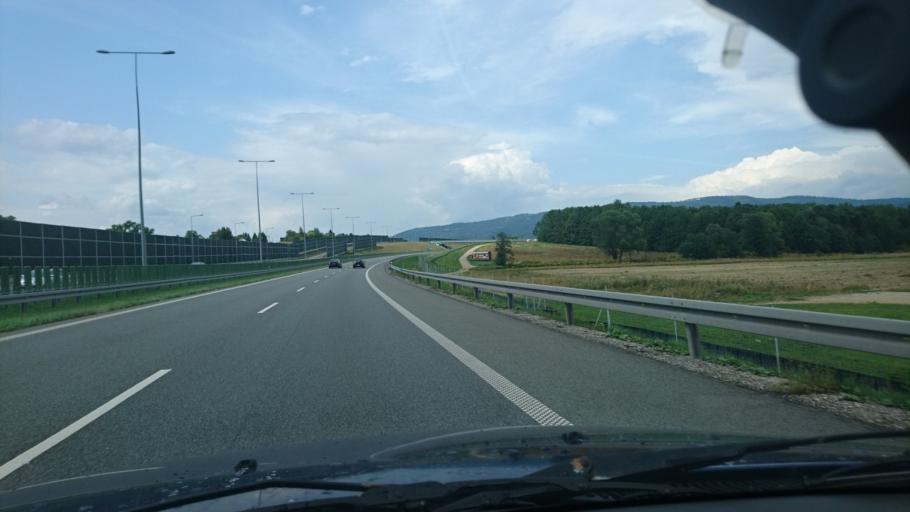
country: PL
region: Silesian Voivodeship
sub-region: Powiat zywiecki
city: Lodygowice
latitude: 49.7075
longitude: 19.1209
